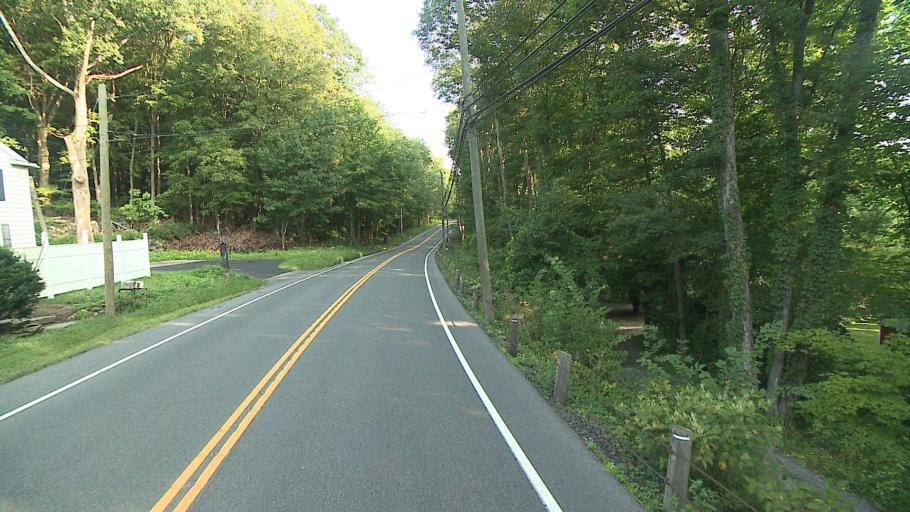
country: US
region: Connecticut
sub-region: Fairfield County
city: Sherman
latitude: 41.6006
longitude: -73.4587
